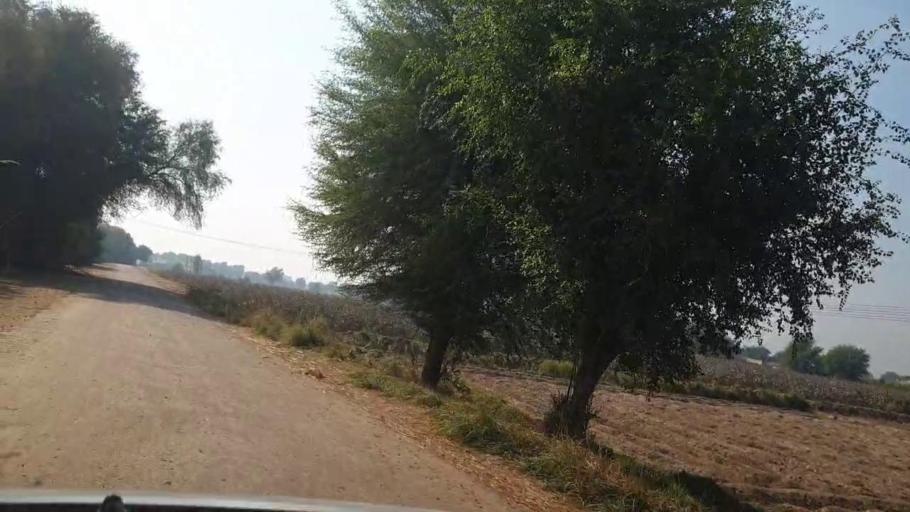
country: PK
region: Sindh
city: Bhan
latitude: 26.6047
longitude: 67.7436
